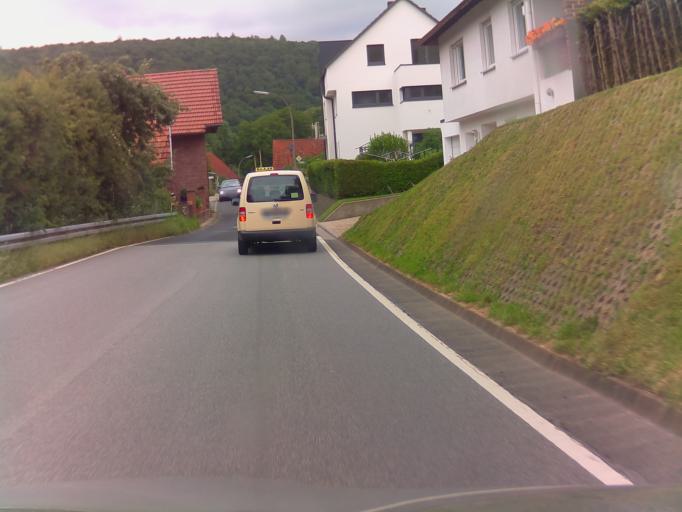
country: DE
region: Bavaria
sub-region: Regierungsbezirk Unterfranken
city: Schonau
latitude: 50.0952
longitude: 9.7336
